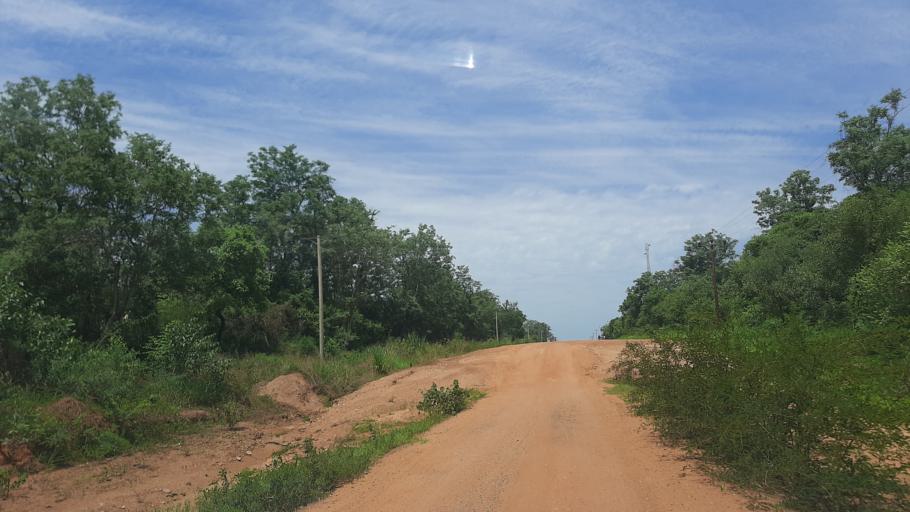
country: ET
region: Gambela
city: Gambela
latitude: 8.0657
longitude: 34.5867
